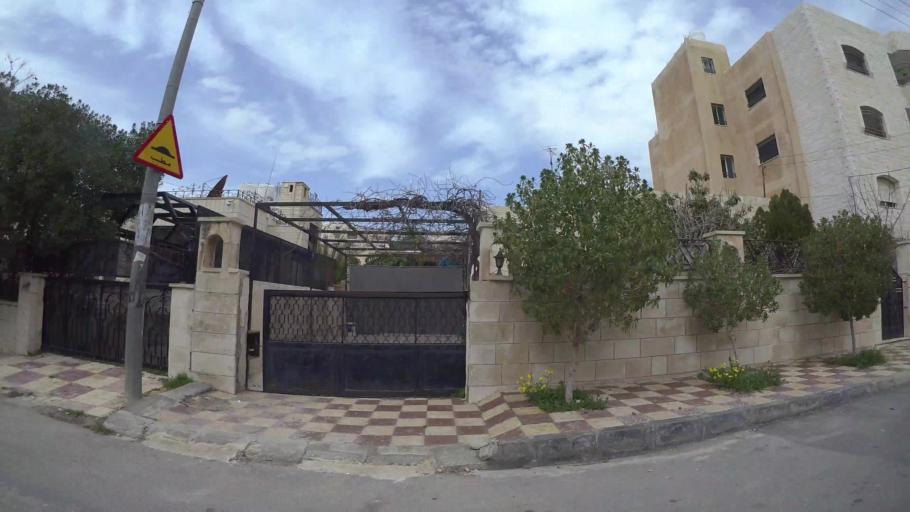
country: JO
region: Amman
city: Amman
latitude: 31.9956
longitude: 35.9444
